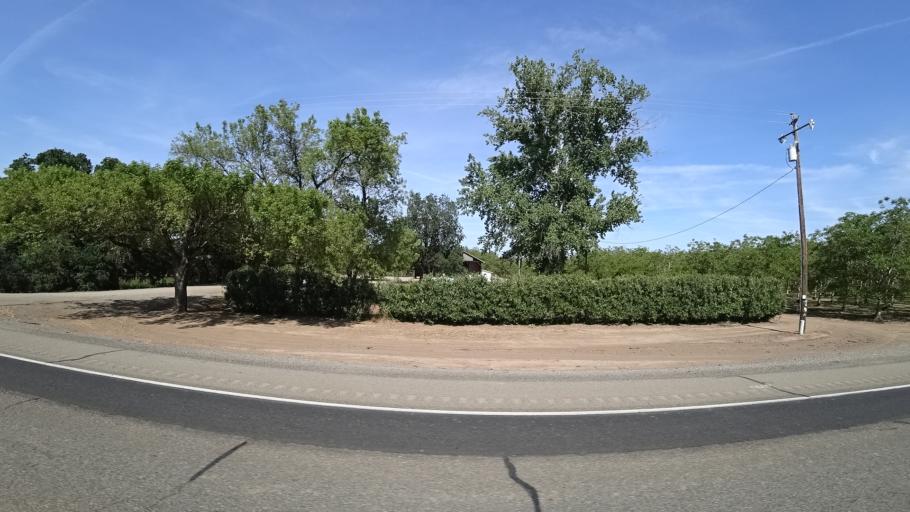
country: US
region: California
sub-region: Tehama County
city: Los Molinos
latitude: 39.9811
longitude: -122.0795
